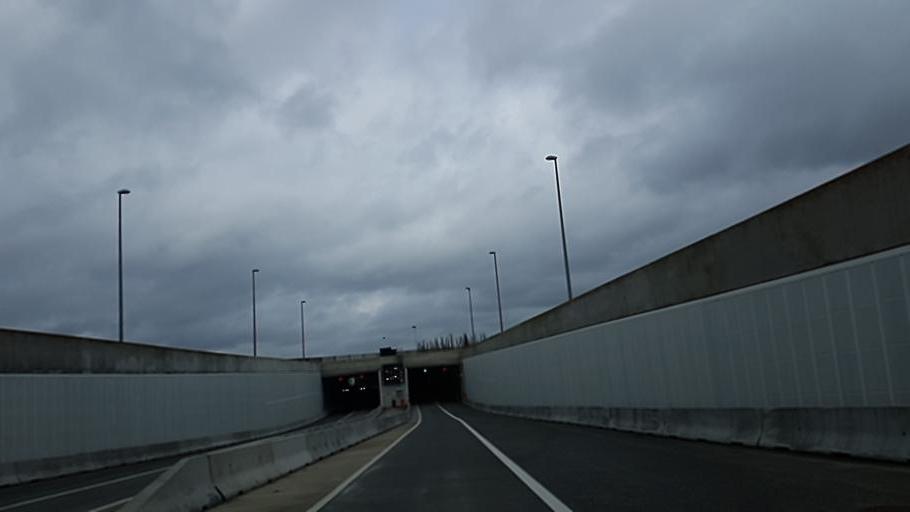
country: BE
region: Flanders
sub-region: Provincie Antwerpen
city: Borsbeek
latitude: 51.1851
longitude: 4.4710
